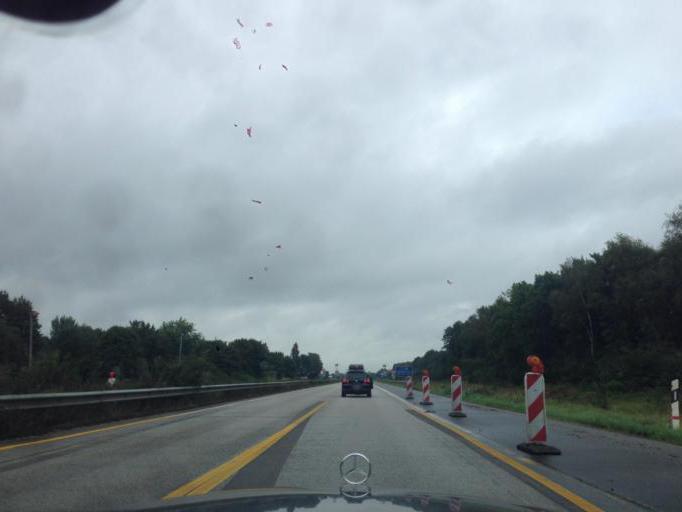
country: DE
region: Schleswig-Holstein
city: Padenstedt
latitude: 54.0214
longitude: 9.9321
